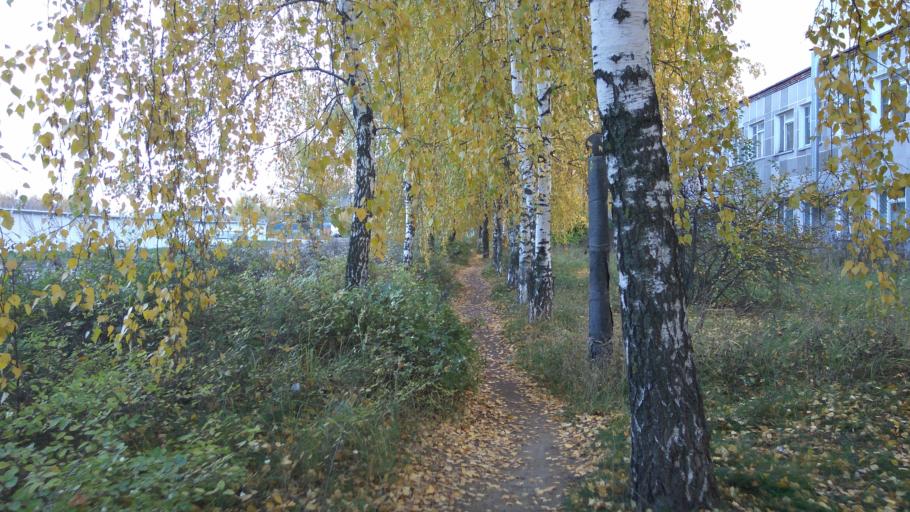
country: RU
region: Tatarstan
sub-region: Gorod Kazan'
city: Kazan
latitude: 55.7312
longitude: 49.1098
